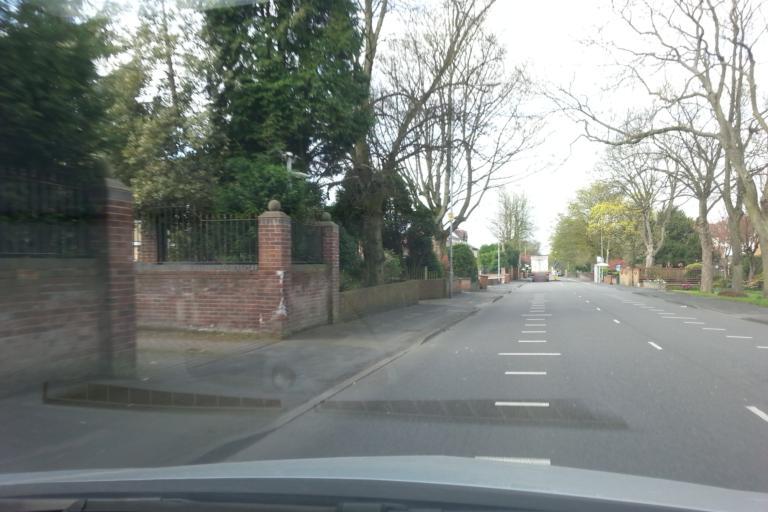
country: GB
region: England
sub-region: Walsall
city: Walsall
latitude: 52.5924
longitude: -1.9646
